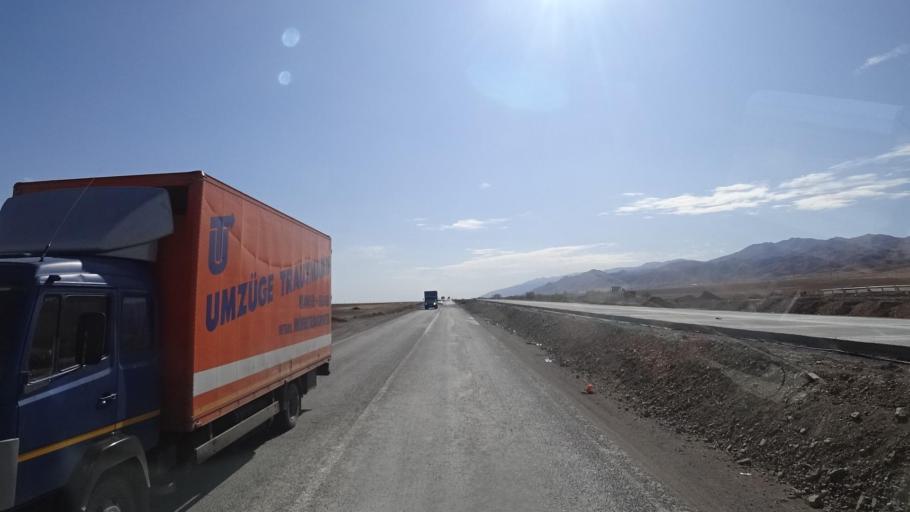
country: KG
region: Chuy
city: Ivanovka
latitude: 43.3996
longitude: 75.1164
